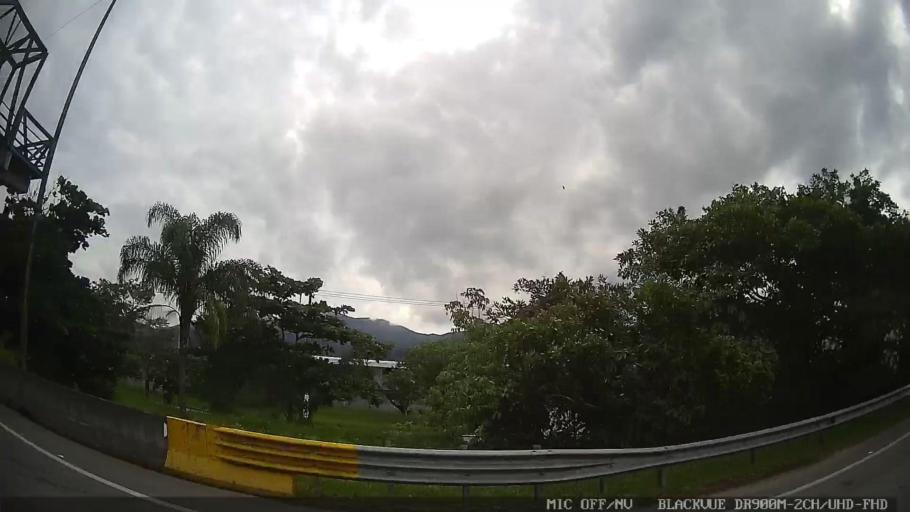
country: BR
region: Sao Paulo
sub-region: Sao Vicente
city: Sao Vicente
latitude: -23.9616
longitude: -46.4701
